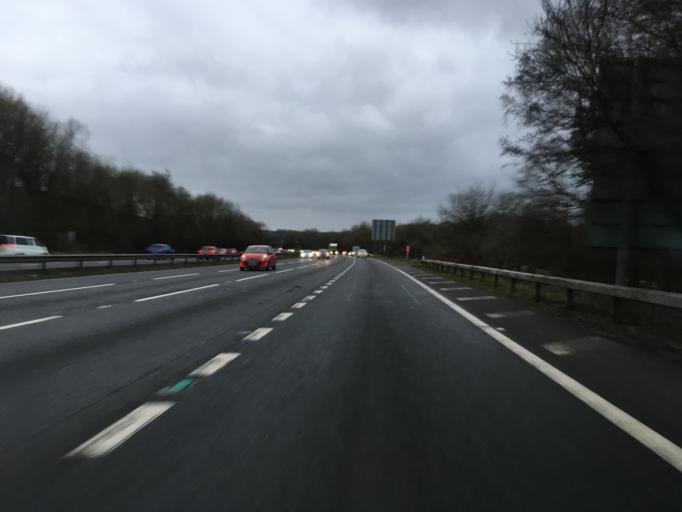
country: GB
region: Wales
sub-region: Cardiff
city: Pentyrch
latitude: 51.5075
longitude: -3.3266
